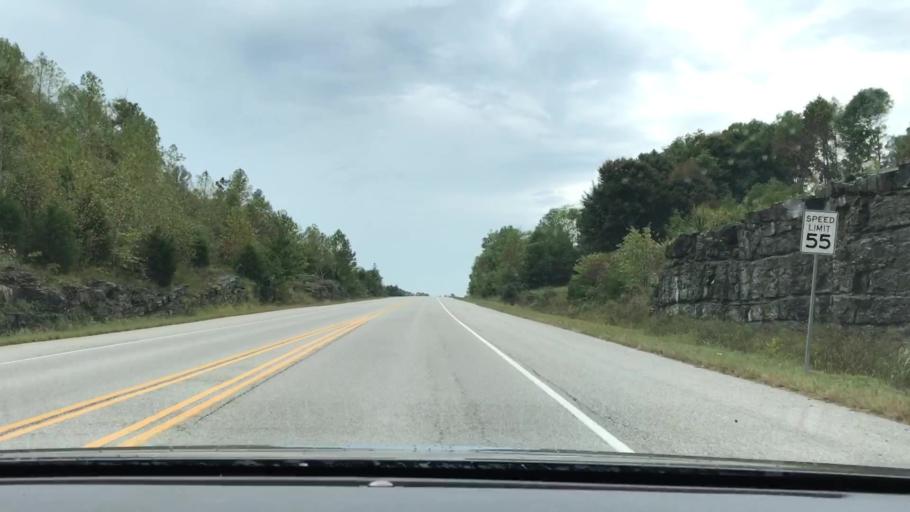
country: US
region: Tennessee
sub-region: Macon County
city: Red Boiling Springs
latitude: 36.5306
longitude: -85.8279
